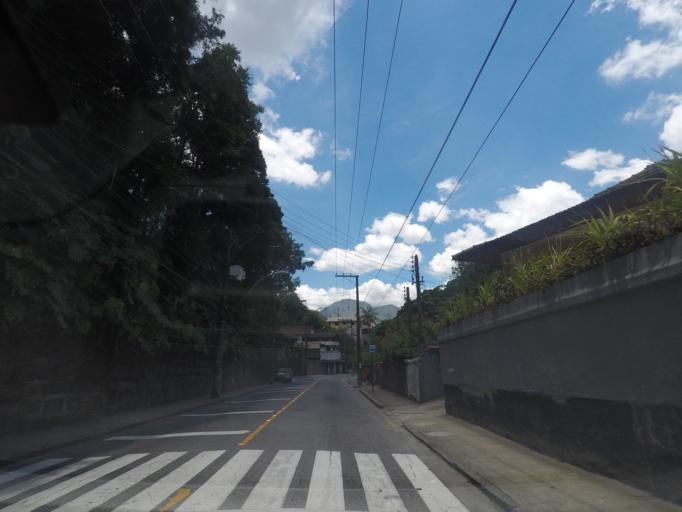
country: BR
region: Rio de Janeiro
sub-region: Petropolis
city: Petropolis
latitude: -22.5007
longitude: -43.1689
